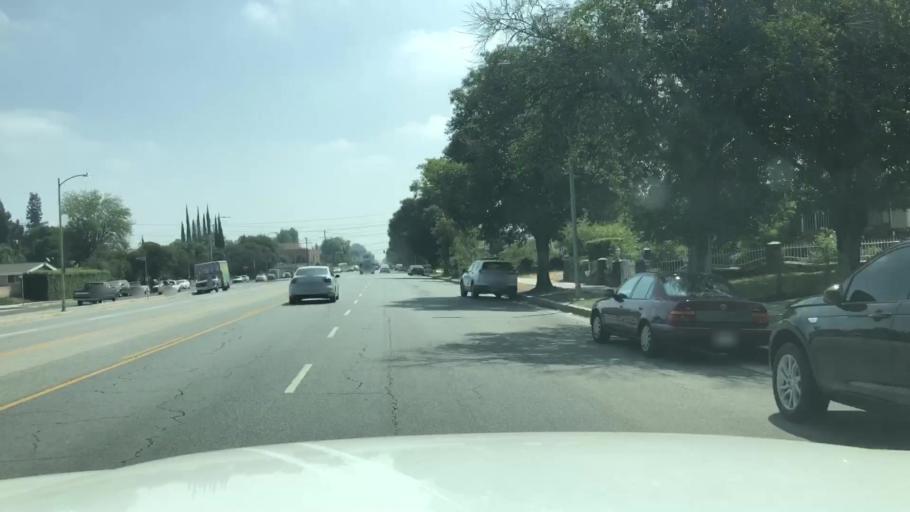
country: US
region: California
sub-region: Los Angeles County
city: Northridge
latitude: 34.1865
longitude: -118.5480
